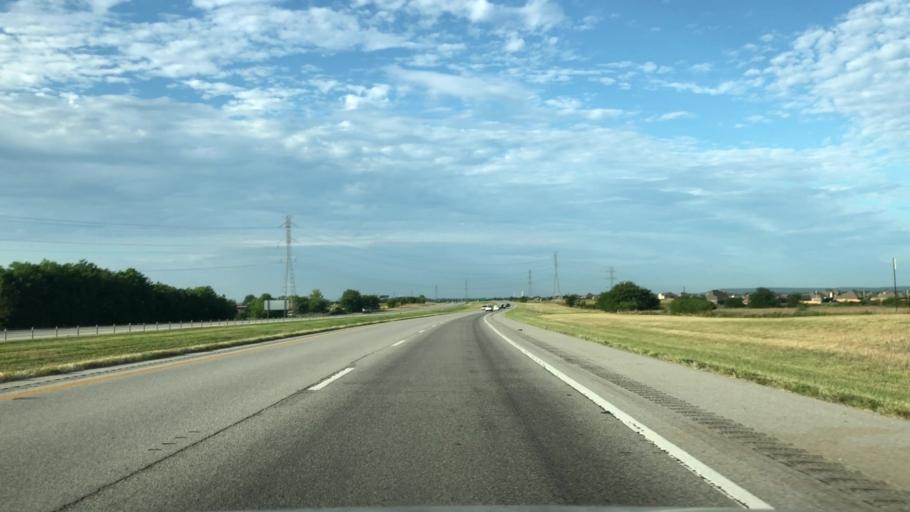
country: US
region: Oklahoma
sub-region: Osage County
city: Skiatook
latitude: 36.3491
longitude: -95.9216
